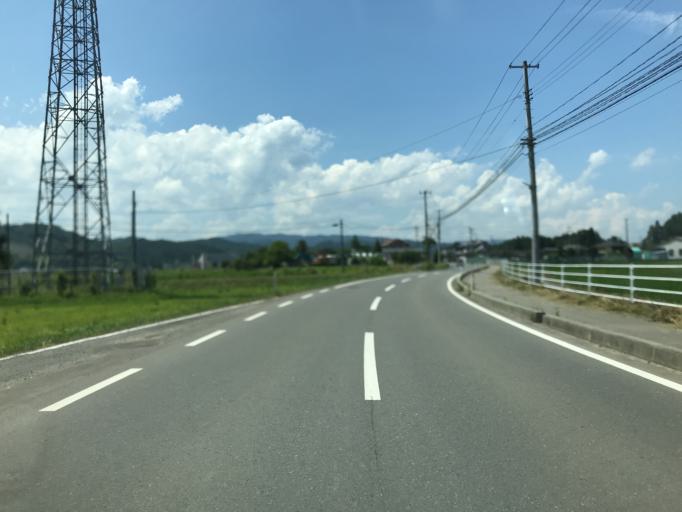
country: JP
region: Fukushima
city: Namie
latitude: 37.7183
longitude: 140.9324
